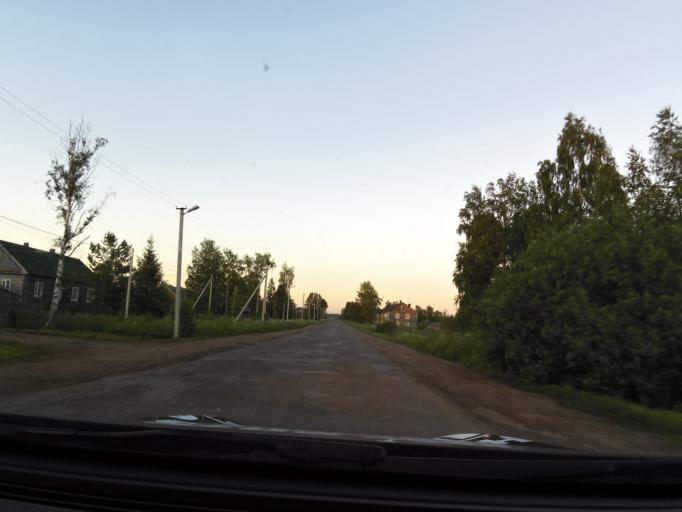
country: RU
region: Leningrad
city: Voznesen'ye
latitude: 60.8503
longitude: 35.5616
